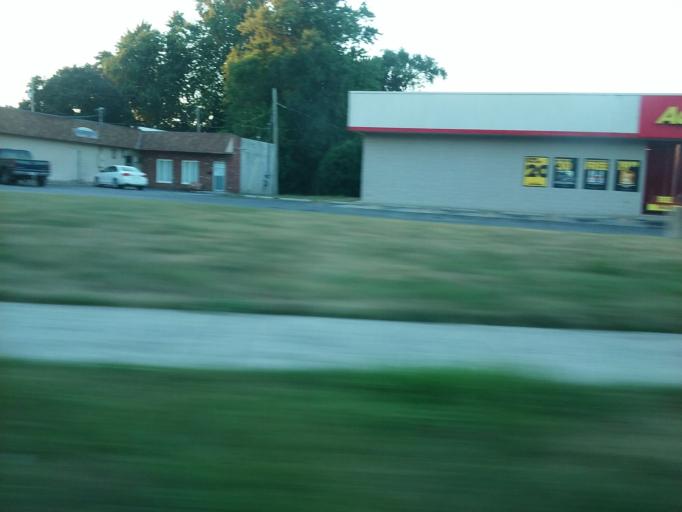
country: US
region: Ohio
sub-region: Hancock County
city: Findlay
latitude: 41.0481
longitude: -83.6332
